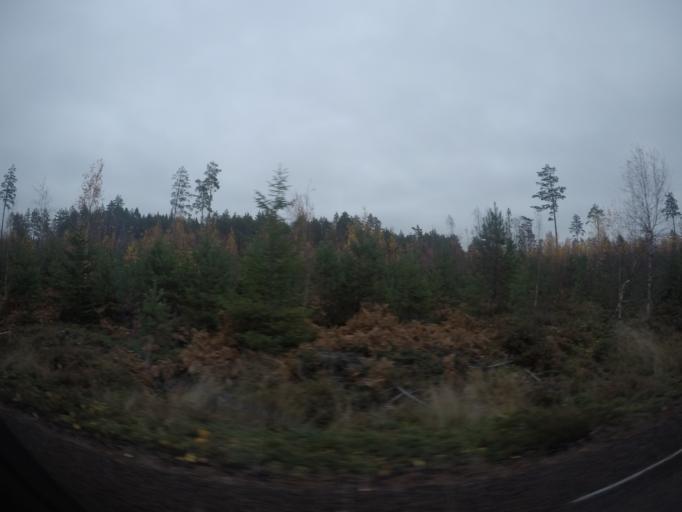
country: SE
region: Vaestmanland
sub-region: Surahammars Kommun
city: Surahammar
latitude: 59.6647
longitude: 16.0827
